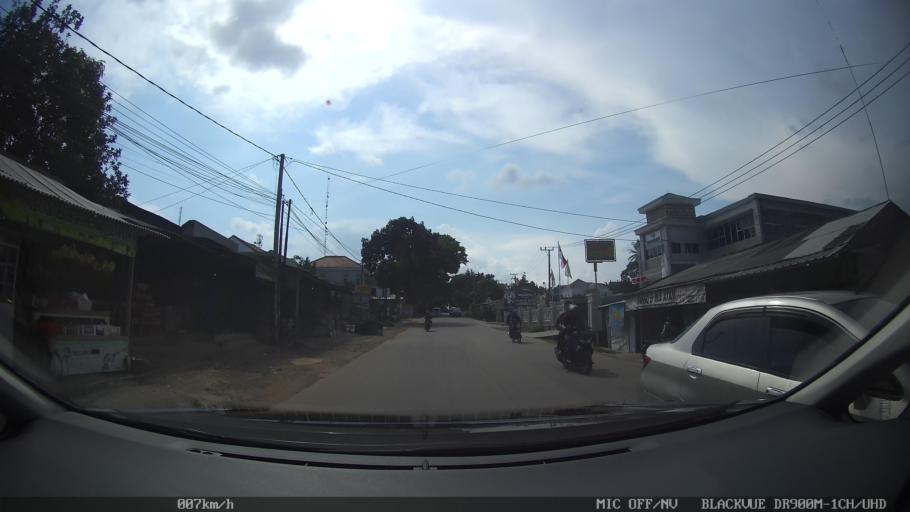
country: ID
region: Lampung
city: Bandarlampung
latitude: -5.4085
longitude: 105.2221
